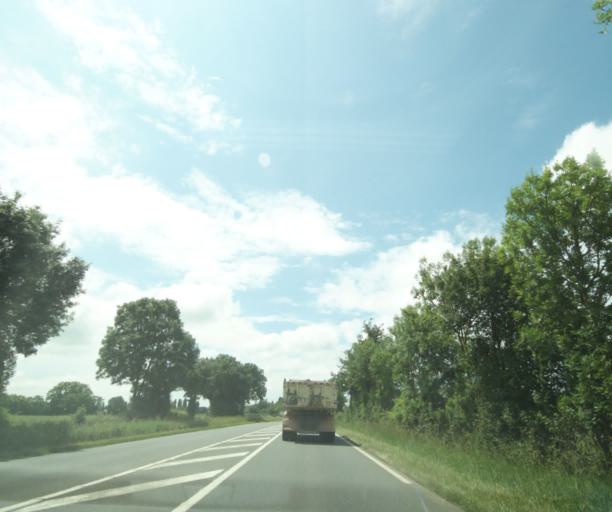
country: FR
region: Poitou-Charentes
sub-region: Departement des Deux-Sevres
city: Champdeniers-Saint-Denis
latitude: 46.4730
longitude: -0.3637
